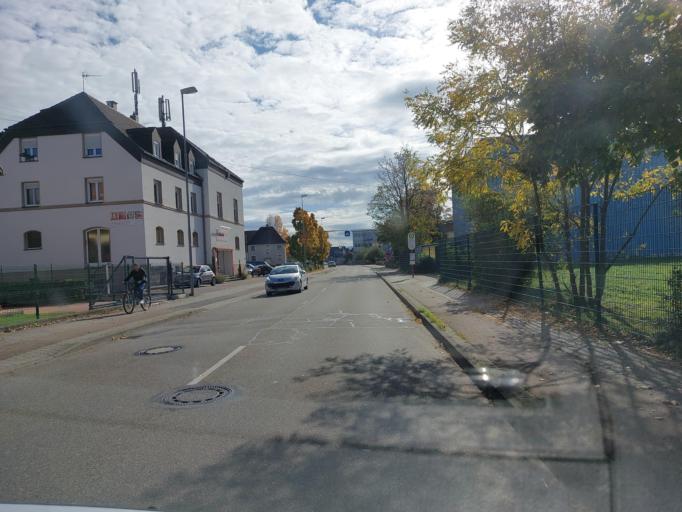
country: DE
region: Baden-Wuerttemberg
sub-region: Freiburg Region
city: Teningen
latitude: 48.1342
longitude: 7.8057
